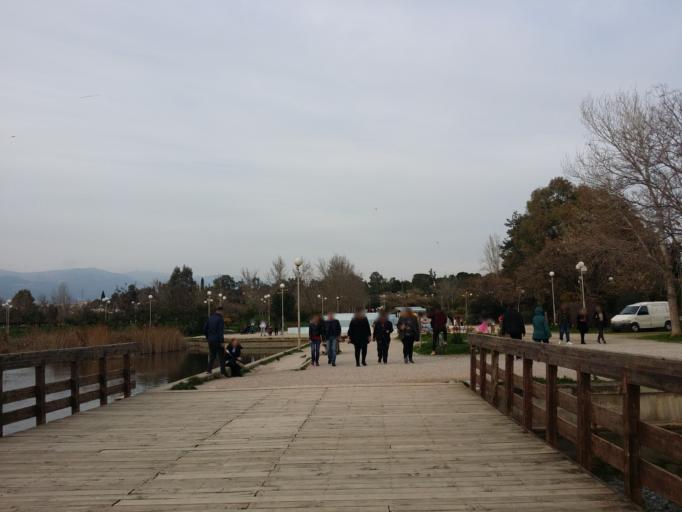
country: GR
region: Attica
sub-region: Nomarchia Athinas
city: Agioi Anargyroi
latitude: 38.0439
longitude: 23.7216
